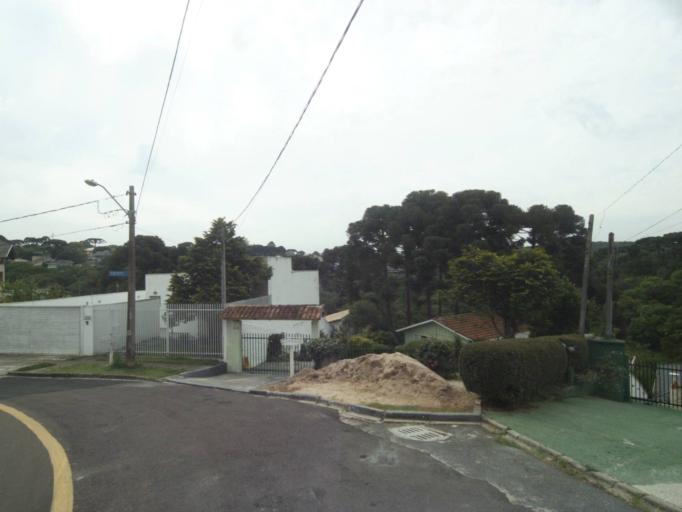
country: BR
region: Parana
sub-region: Curitiba
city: Curitiba
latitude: -25.3985
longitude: -49.3023
